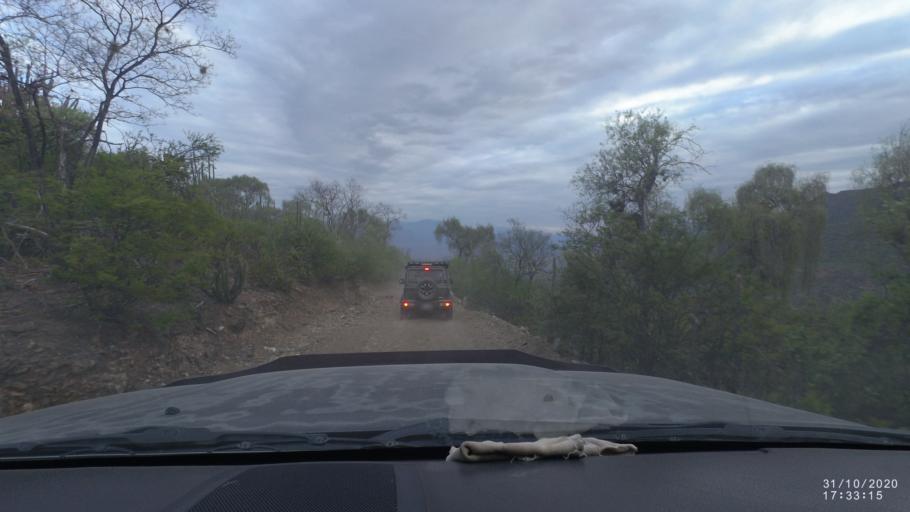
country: BO
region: Chuquisaca
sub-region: Provincia Zudanez
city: Mojocoya
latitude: -18.5996
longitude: -64.5507
